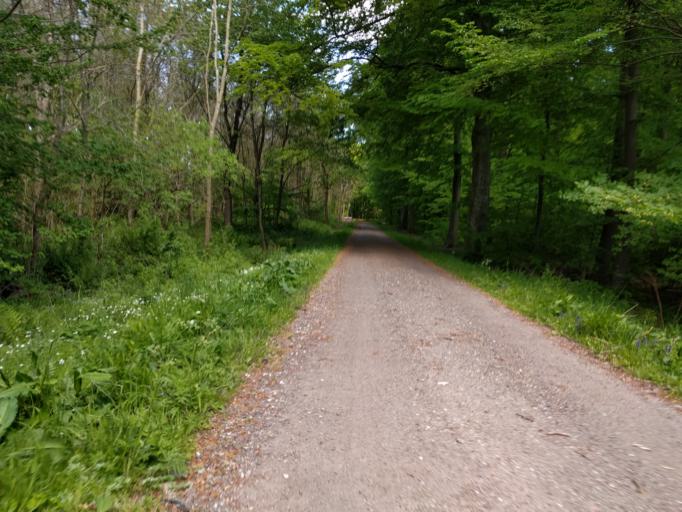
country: DK
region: Zealand
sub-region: Guldborgsund Kommune
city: Stubbekobing
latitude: 54.8030
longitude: 12.1095
